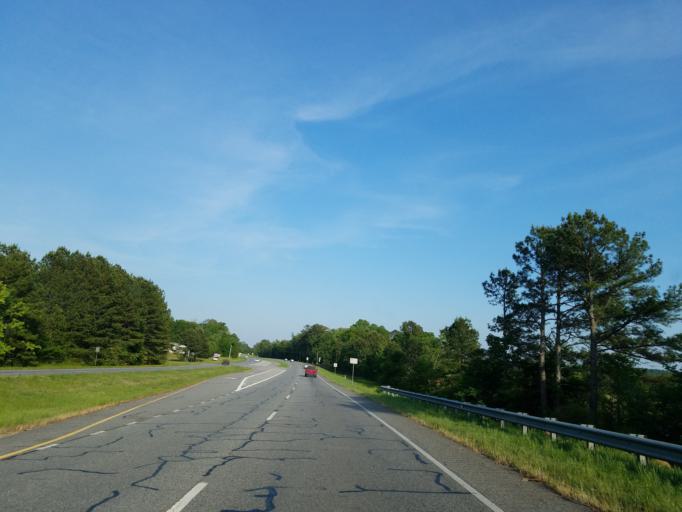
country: US
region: Georgia
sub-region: Floyd County
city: Rome
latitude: 34.4013
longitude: -85.2139
